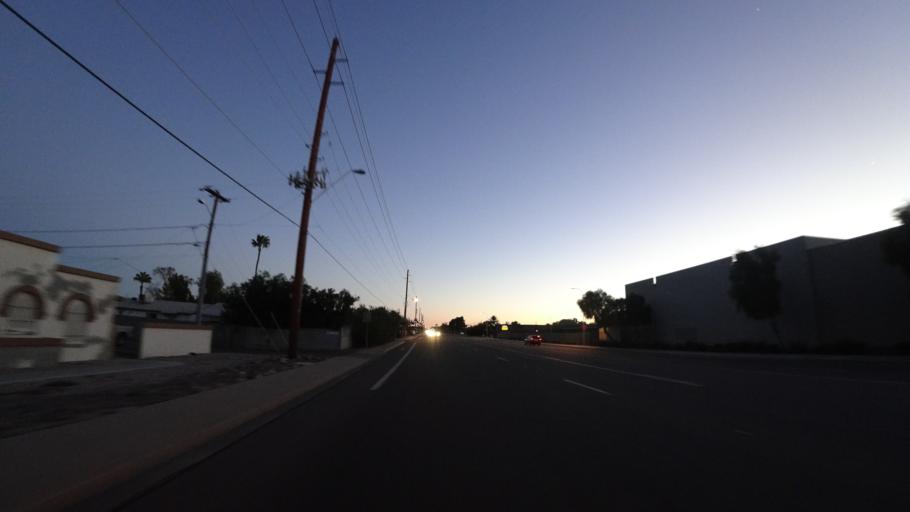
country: US
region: Arizona
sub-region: Maricopa County
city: Tempe Junction
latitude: 33.4210
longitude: -111.9608
